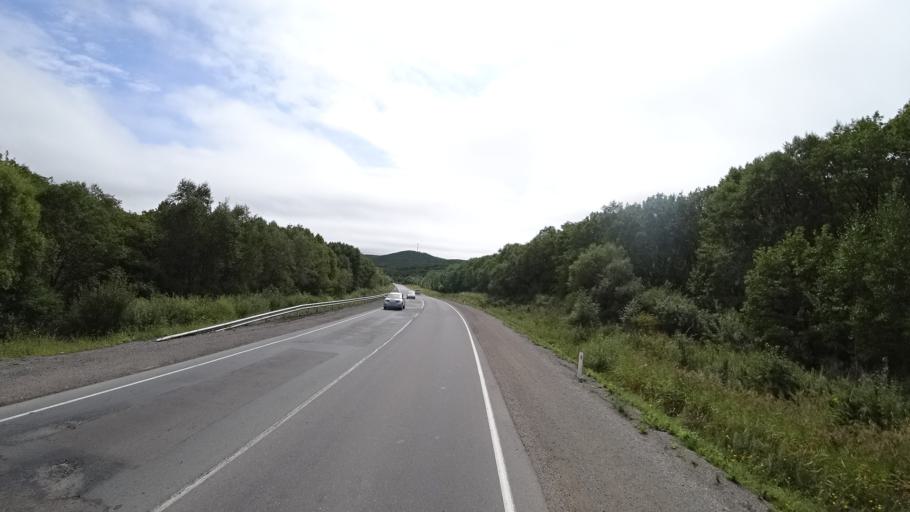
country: RU
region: Primorskiy
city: Lyalichi
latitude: 44.1206
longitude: 132.4200
